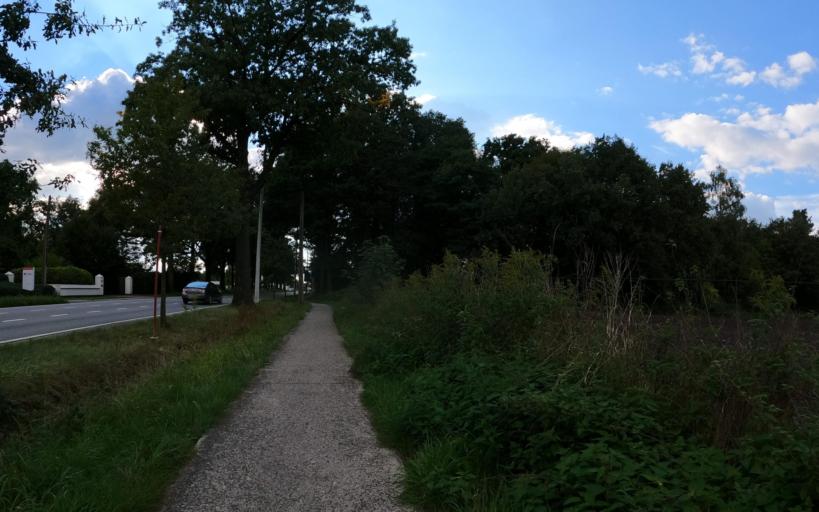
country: BE
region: Flanders
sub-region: Provincie Antwerpen
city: Oostmalle
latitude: 51.2991
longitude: 4.7159
